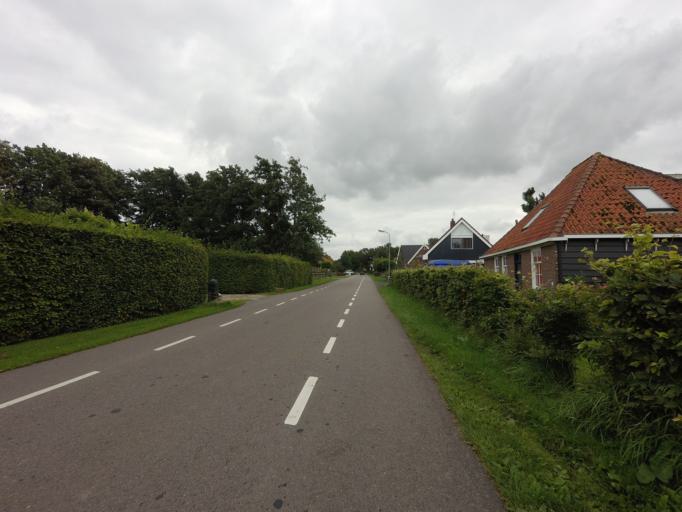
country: NL
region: North Holland
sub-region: Gemeente Edam-Volendam
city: Edam
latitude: 52.5403
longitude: 5.0130
